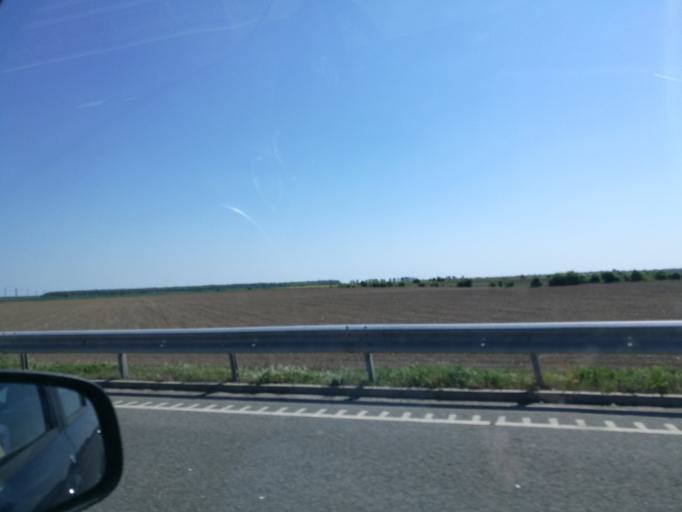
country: RO
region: Ilfov
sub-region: Comuna Moara Vlasiei
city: Caciulati
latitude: 44.6166
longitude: 26.1847
